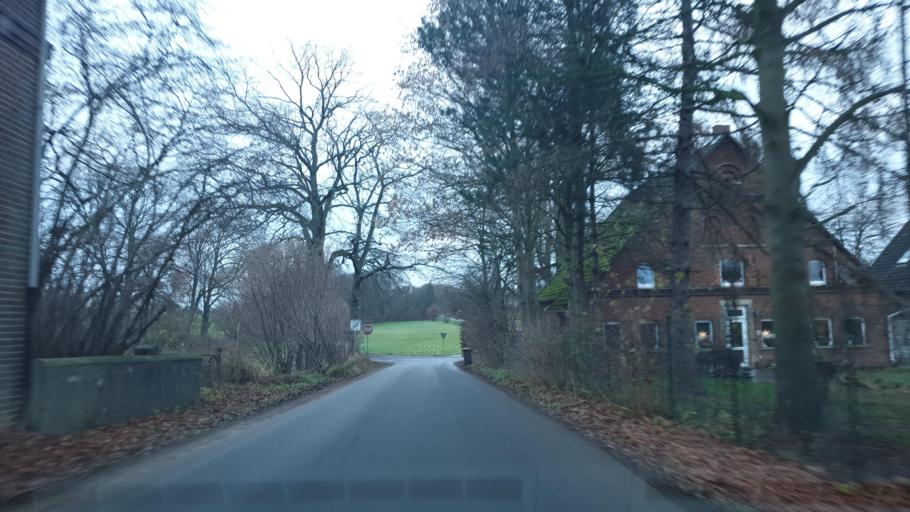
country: DE
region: North Rhine-Westphalia
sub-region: Regierungsbezirk Detmold
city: Hiddenhausen
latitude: 52.1455
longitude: 8.6352
